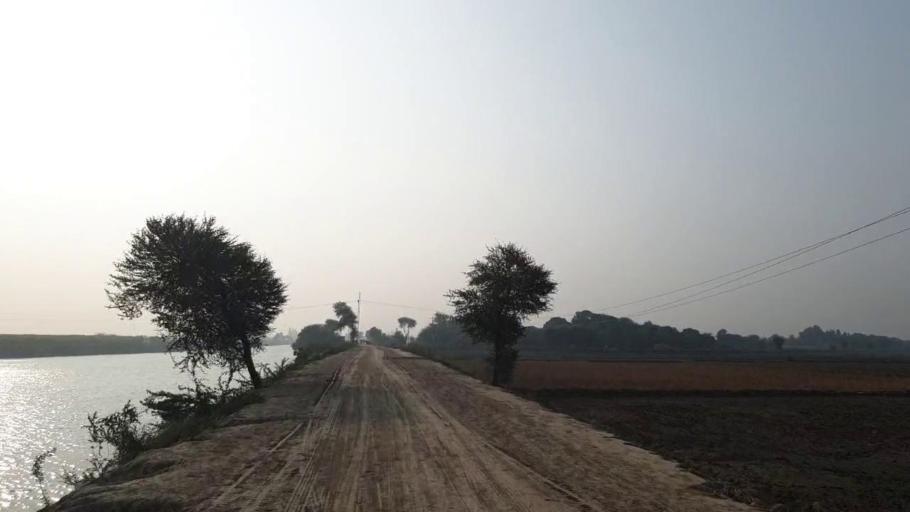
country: PK
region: Sindh
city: Tando Muhammad Khan
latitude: 25.1003
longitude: 68.5747
